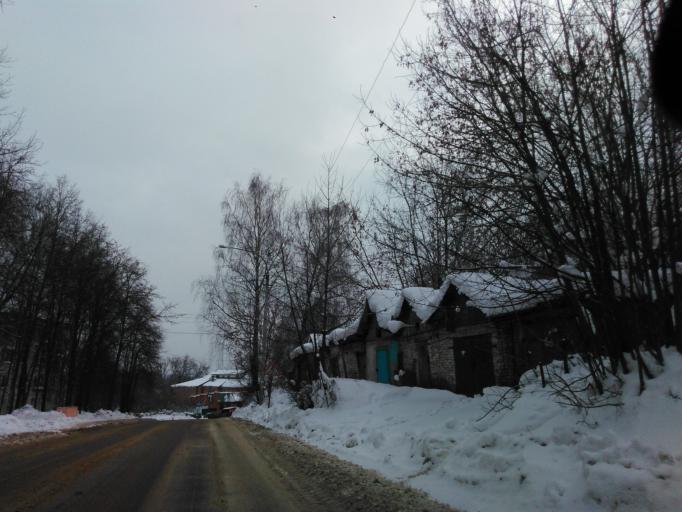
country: RU
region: Moskovskaya
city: Yakhroma
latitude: 56.2826
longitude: 37.4836
